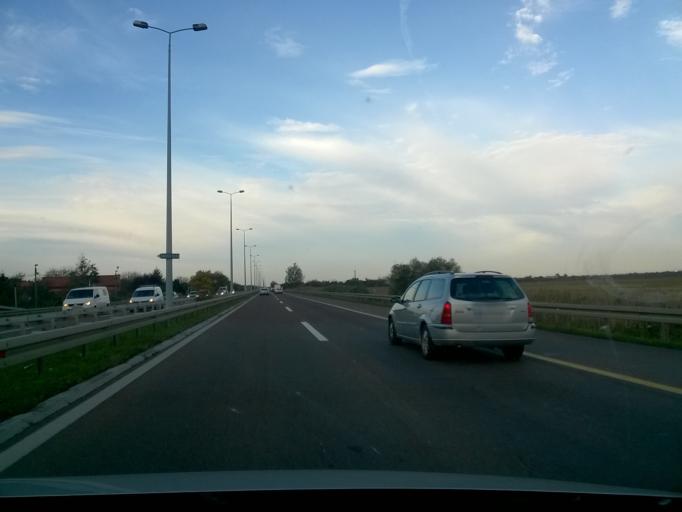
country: RS
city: Ovca
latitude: 44.8604
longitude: 20.5674
